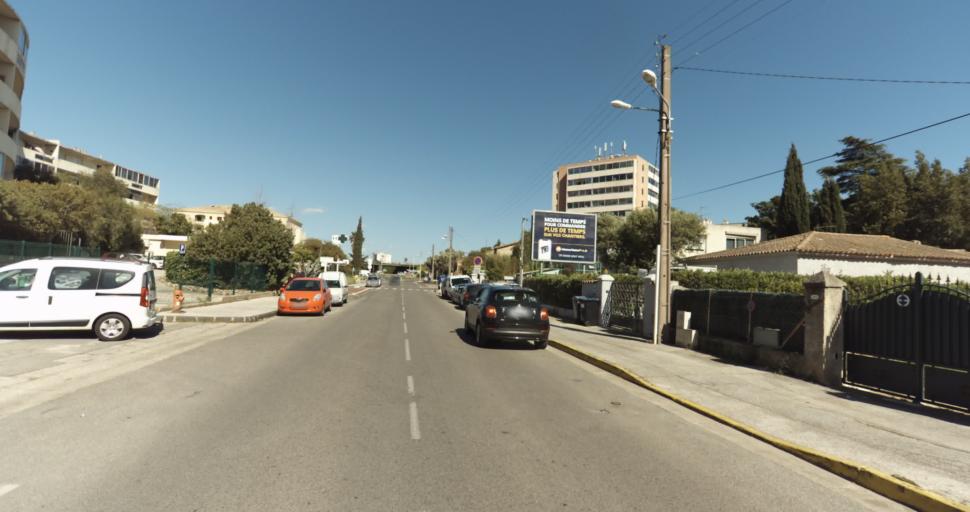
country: FR
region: Provence-Alpes-Cote d'Azur
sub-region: Departement du Var
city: La Valette-du-Var
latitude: 43.1322
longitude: 5.9789
